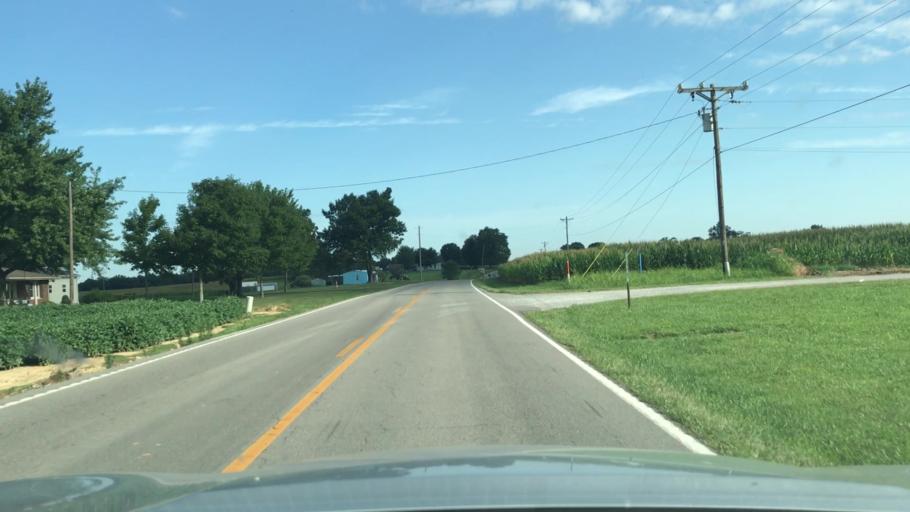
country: US
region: Kentucky
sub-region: Todd County
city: Elkton
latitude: 36.8726
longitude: -87.1655
